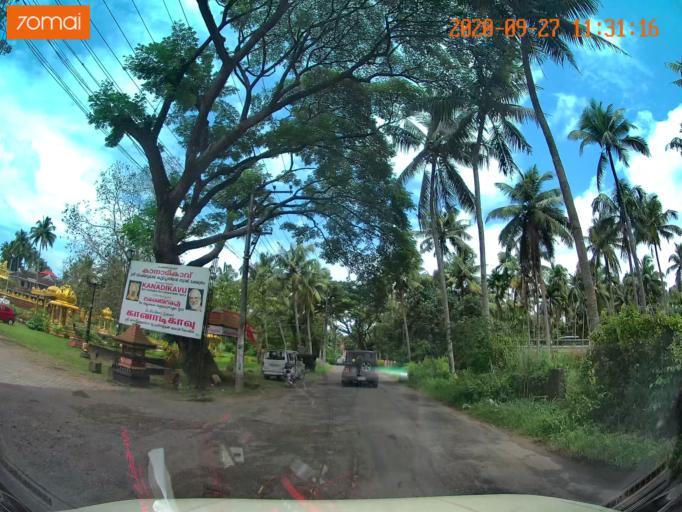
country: IN
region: Kerala
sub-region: Thrissur District
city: Thanniyam
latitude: 10.4221
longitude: 76.1329
